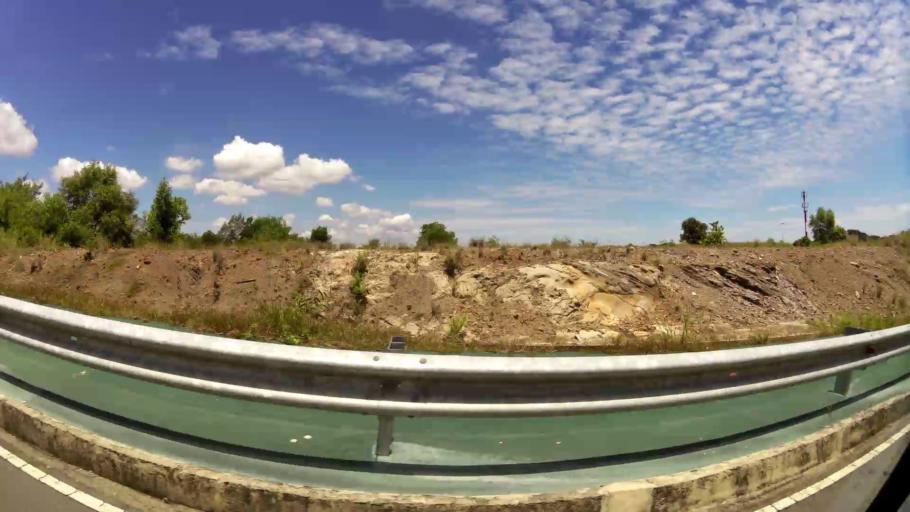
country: BN
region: Brunei and Muara
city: Bandar Seri Begawan
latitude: 5.0066
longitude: 115.0112
